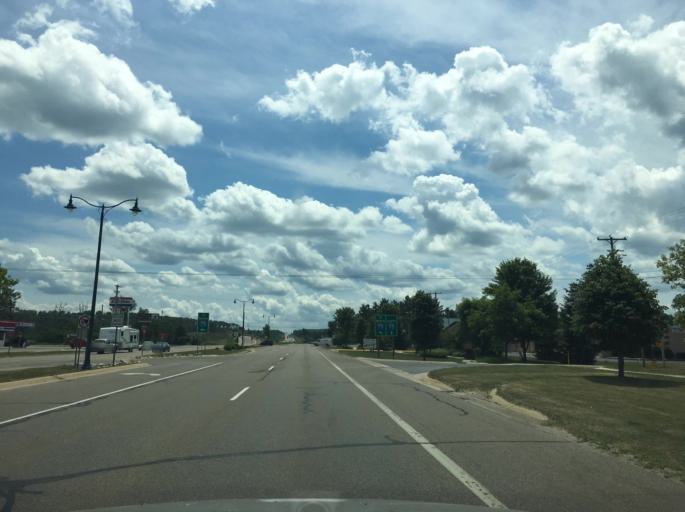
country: US
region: Michigan
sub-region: Crawford County
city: Grayling
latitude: 44.6488
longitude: -84.7088
